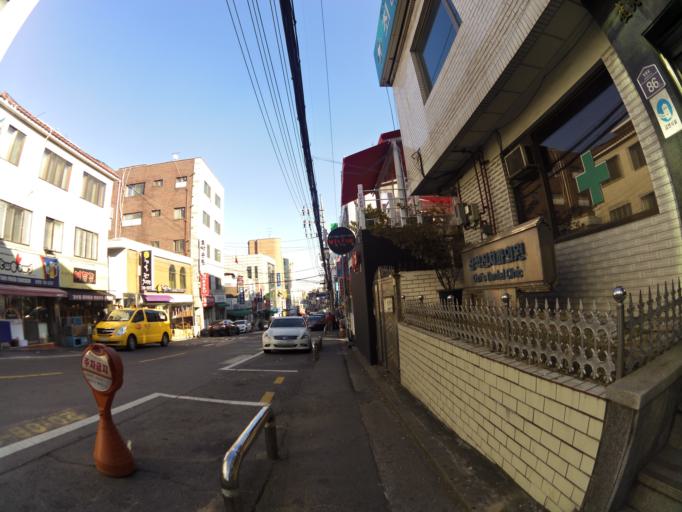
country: KR
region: Seoul
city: Seoul
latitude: 37.5260
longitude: 126.9990
